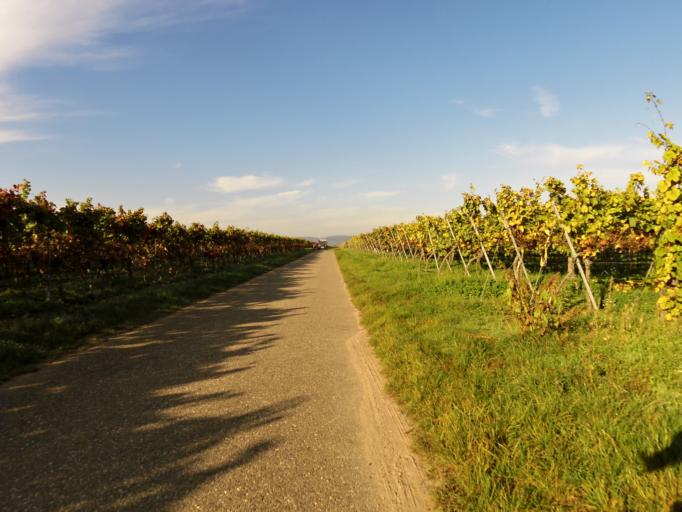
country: DE
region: Rheinland-Pfalz
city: Gonnheim
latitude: 49.4624
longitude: 8.2438
